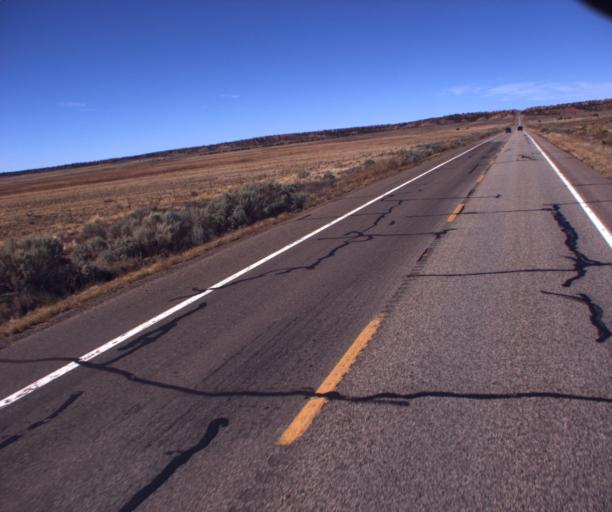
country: US
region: Arizona
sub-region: Mohave County
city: Colorado City
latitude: 36.8730
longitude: -112.8644
